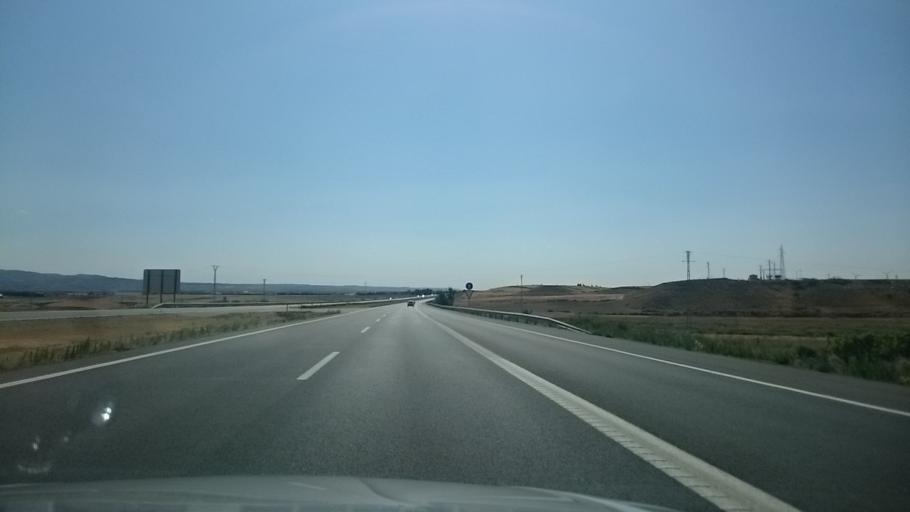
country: ES
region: Aragon
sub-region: Provincia de Zaragoza
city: Gallur
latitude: 41.8327
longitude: -1.3160
